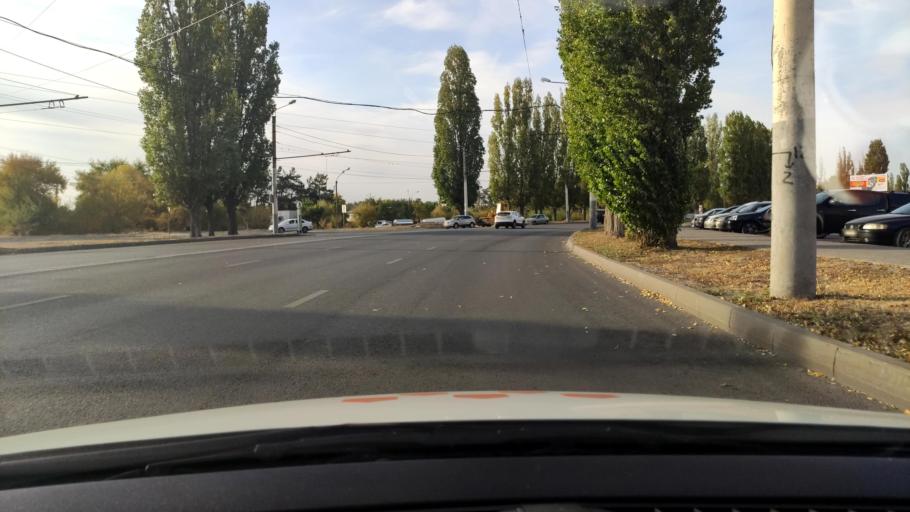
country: RU
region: Voronezj
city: Maslovka
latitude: 51.6019
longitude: 39.2381
